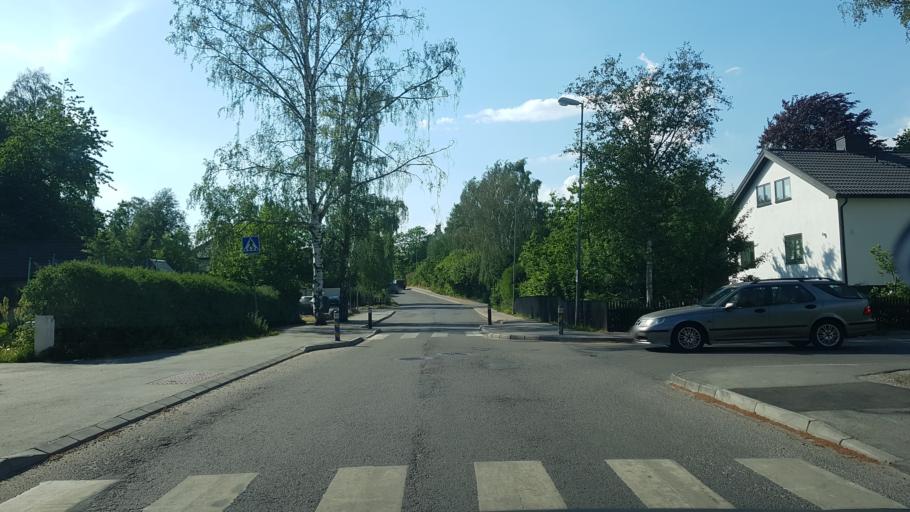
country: SE
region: Stockholm
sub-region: Sollentuna Kommun
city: Sollentuna
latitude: 59.4200
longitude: 17.9710
